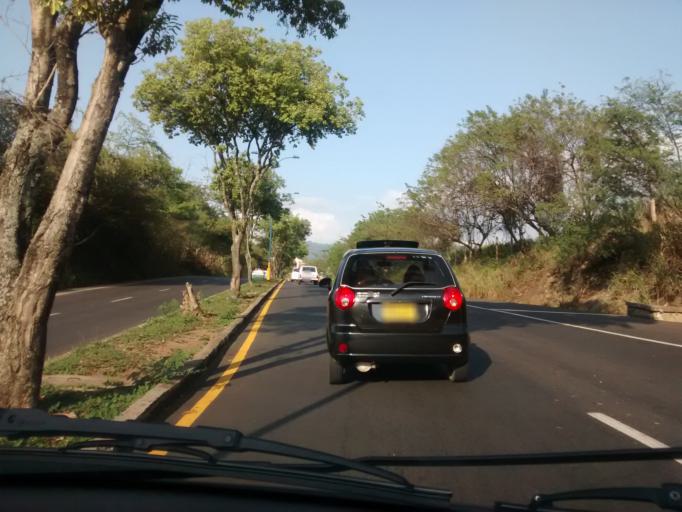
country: CO
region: Santander
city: Bucaramanga
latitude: 7.0902
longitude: -73.1312
